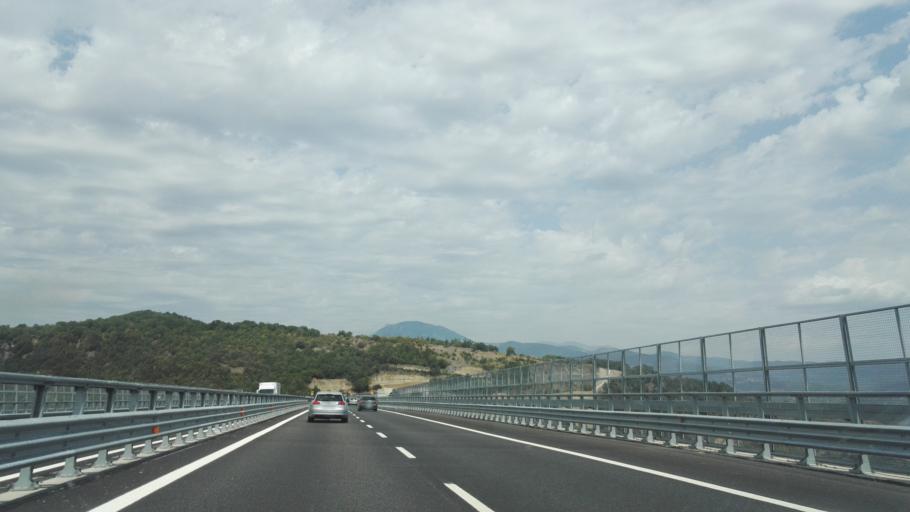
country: IT
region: Calabria
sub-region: Provincia di Cosenza
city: Laino Castello-Nuovo Centro
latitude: 39.9361
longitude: 15.9603
